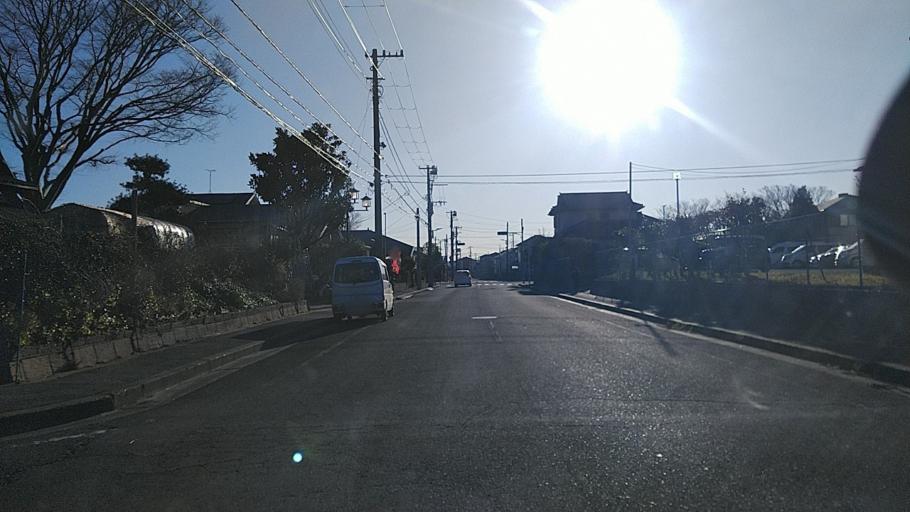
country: JP
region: Chiba
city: Kimitsu
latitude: 35.3295
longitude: 139.8911
